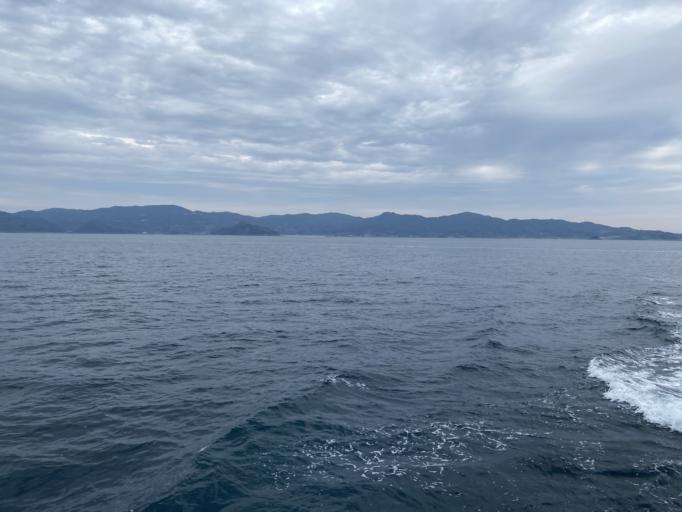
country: JP
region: Nagasaki
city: Nagasaki-shi
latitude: 32.6288
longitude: 129.7431
